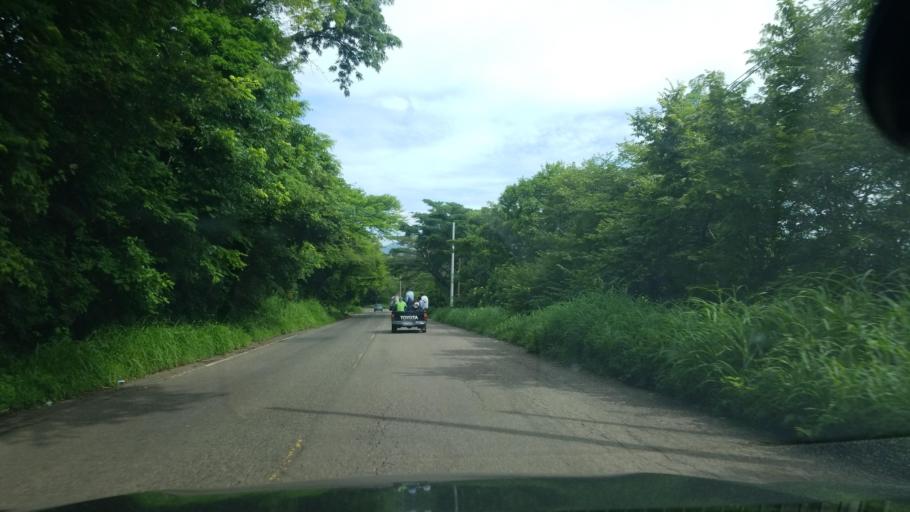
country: HN
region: Choluteca
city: Corpus
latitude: 13.3742
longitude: -87.0440
